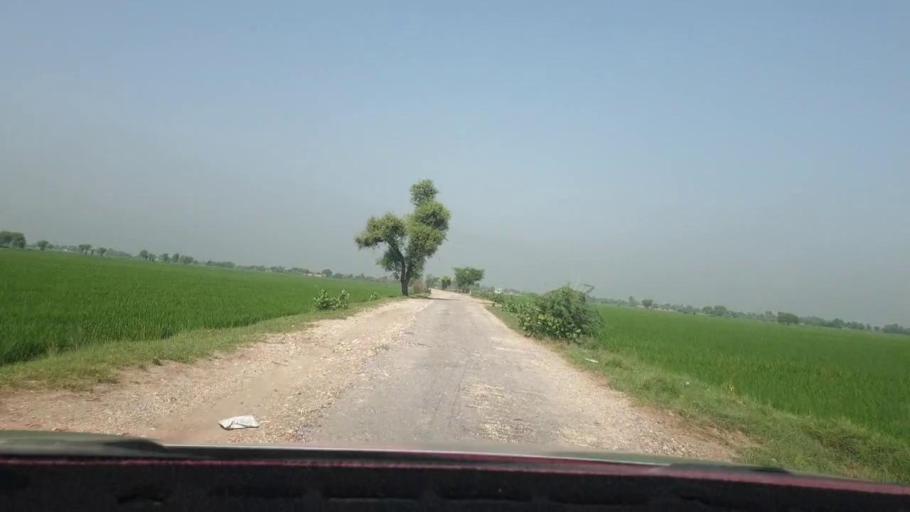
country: PK
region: Sindh
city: Nasirabad
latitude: 27.4306
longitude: 67.9006
